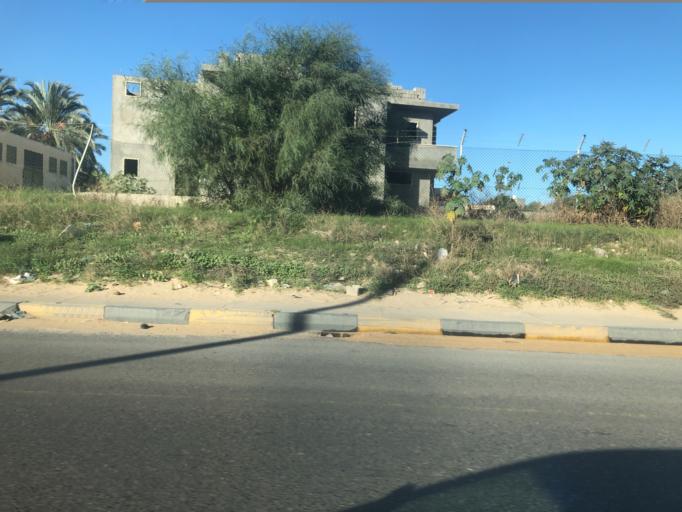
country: LY
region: Tripoli
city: Tagiura
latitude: 32.8692
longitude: 13.2745
